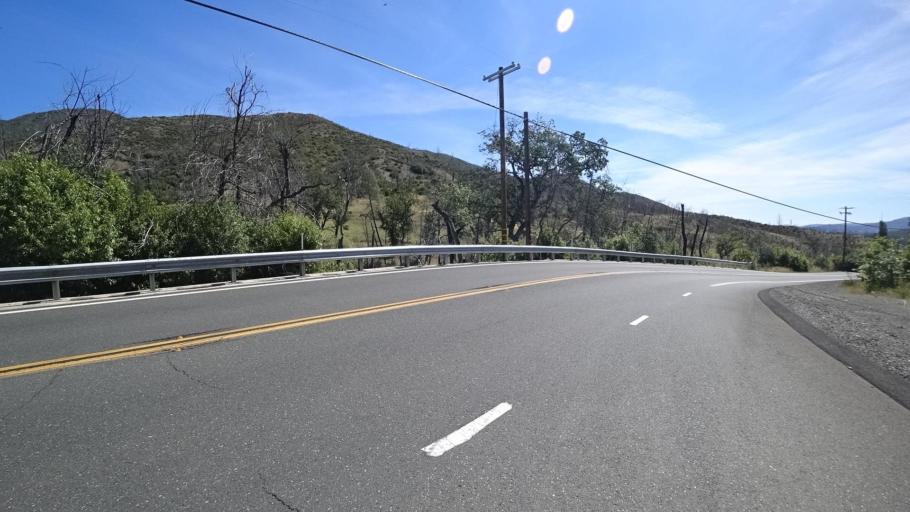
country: US
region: California
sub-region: Lake County
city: Cobb
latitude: 38.7819
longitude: -122.6855
